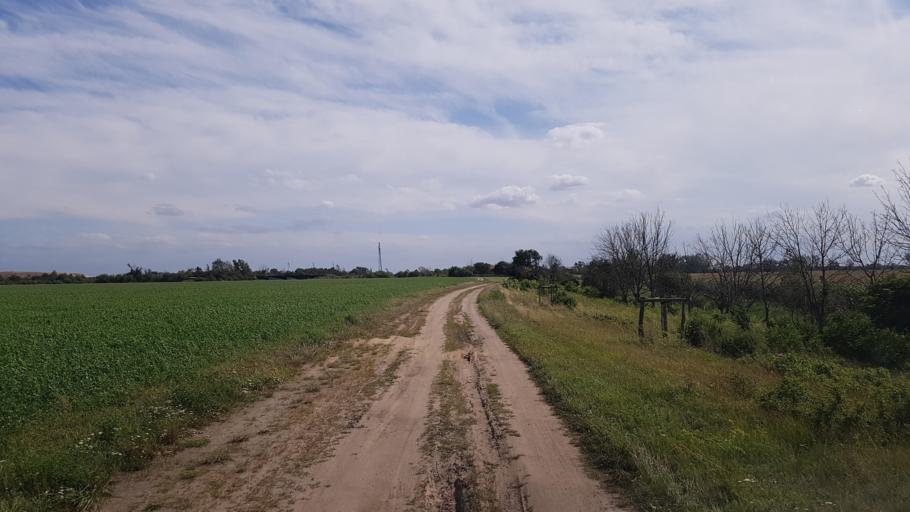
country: DE
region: Brandenburg
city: Muhlberg
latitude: 51.4325
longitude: 13.2598
